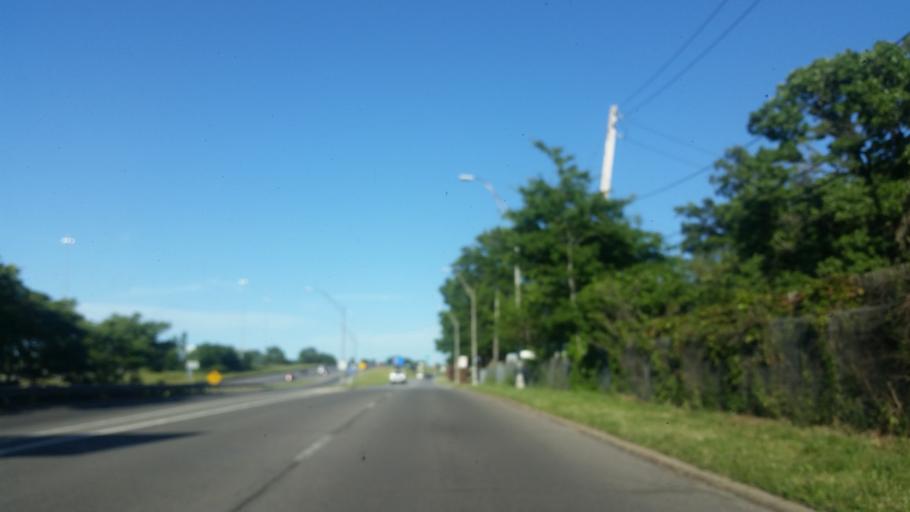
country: US
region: Ohio
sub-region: Cuyahoga County
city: Lakewood
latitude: 41.4688
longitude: -81.7957
